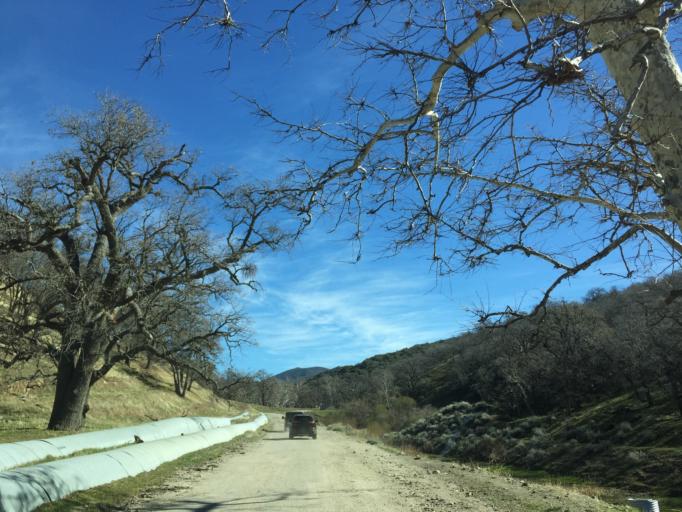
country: US
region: California
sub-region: Kern County
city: Lebec
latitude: 34.8845
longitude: -118.7716
